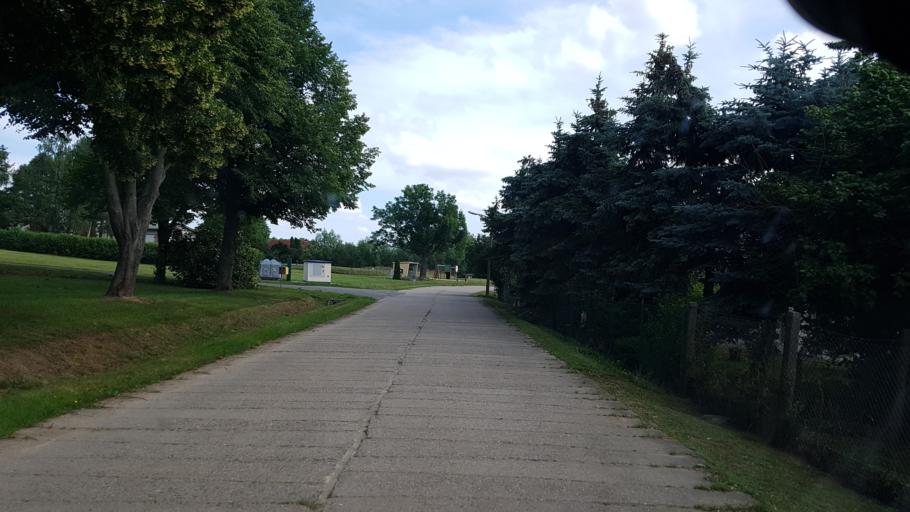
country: DE
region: Brandenburg
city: Prenzlau
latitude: 53.3822
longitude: 13.8065
